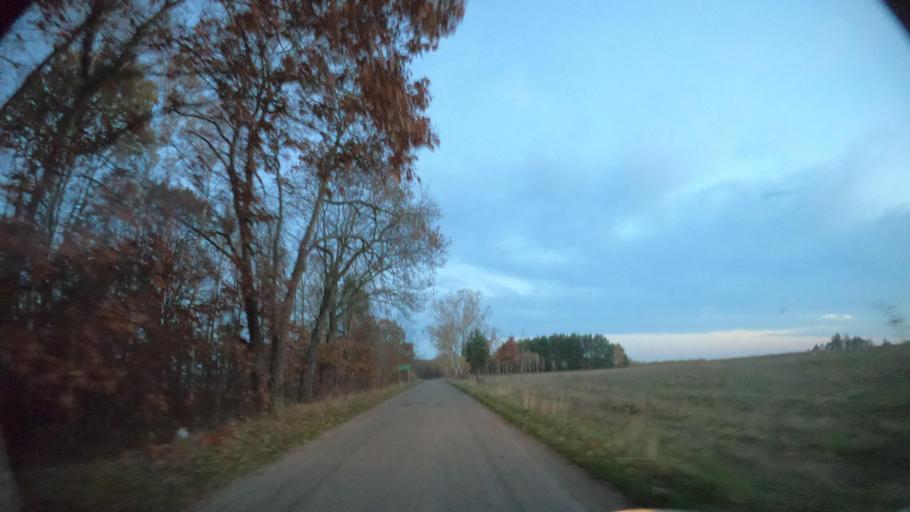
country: PL
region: Greater Poland Voivodeship
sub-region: Powiat zlotowski
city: Sypniewo
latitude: 53.4267
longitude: 16.6538
